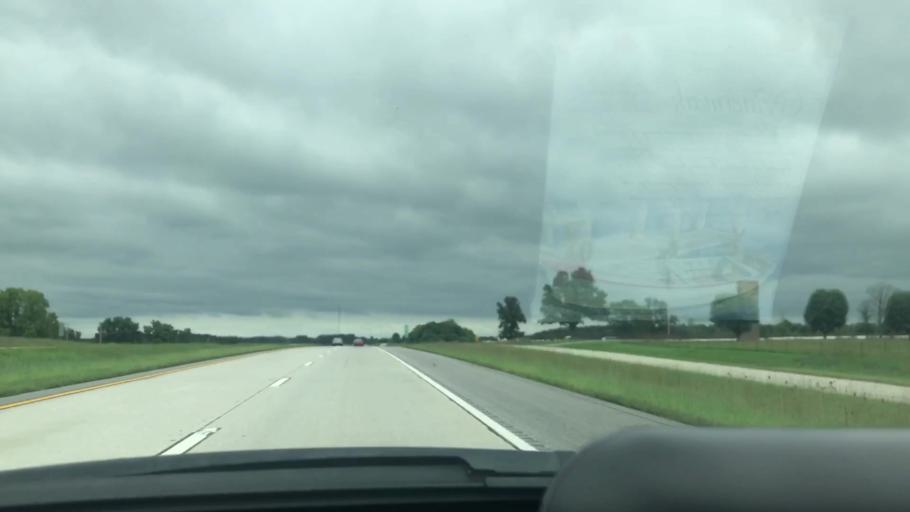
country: US
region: Missouri
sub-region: Greene County
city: Fair Grove
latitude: 37.4362
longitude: -93.1445
